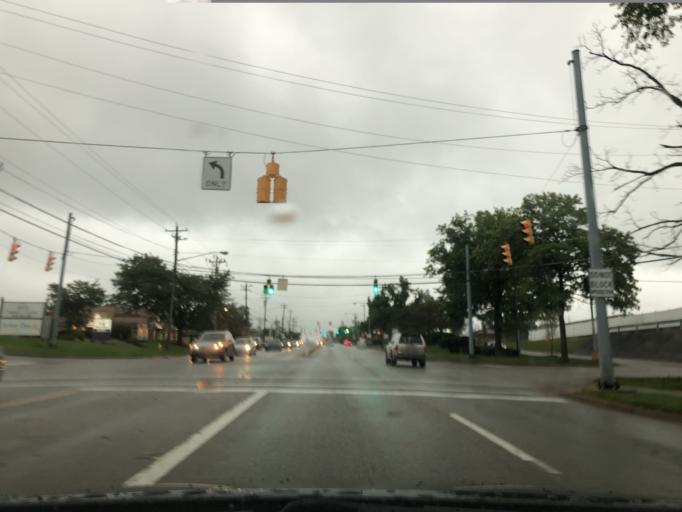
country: US
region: Ohio
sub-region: Hamilton County
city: Dillonvale
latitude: 39.2292
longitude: -84.3946
